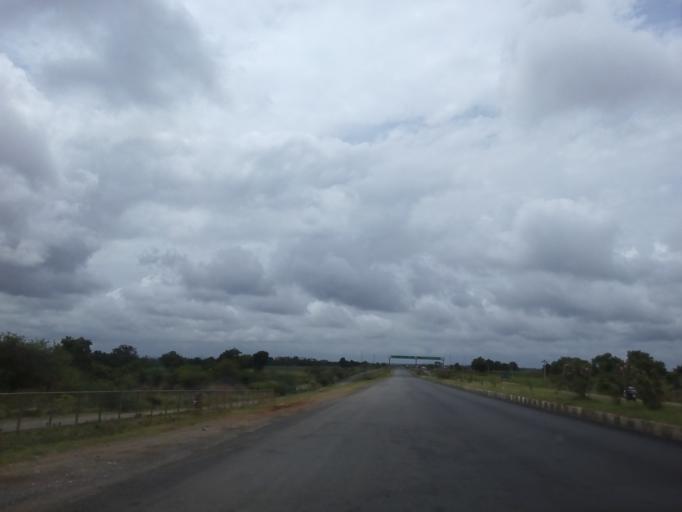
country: IN
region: Karnataka
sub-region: Haveri
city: Byadgi
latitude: 14.6919
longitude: 75.5318
